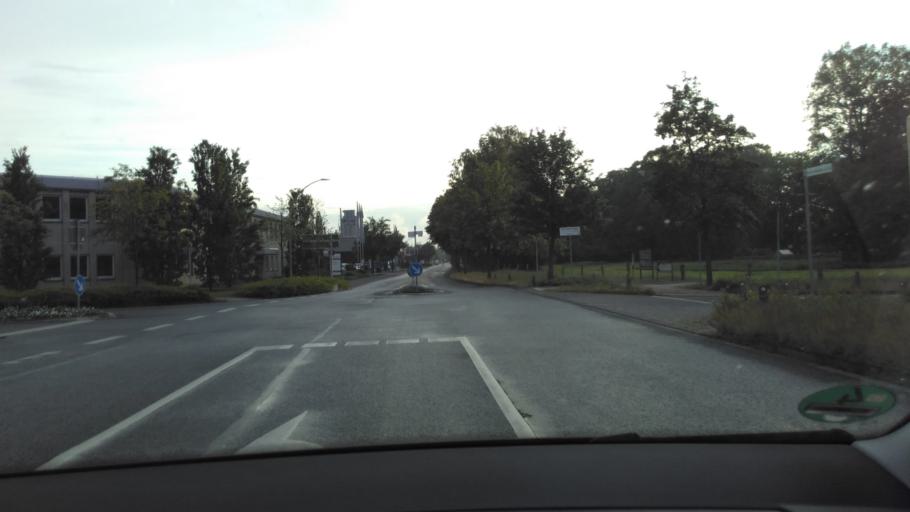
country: DE
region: North Rhine-Westphalia
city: Rietberg
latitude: 51.8238
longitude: 8.4451
